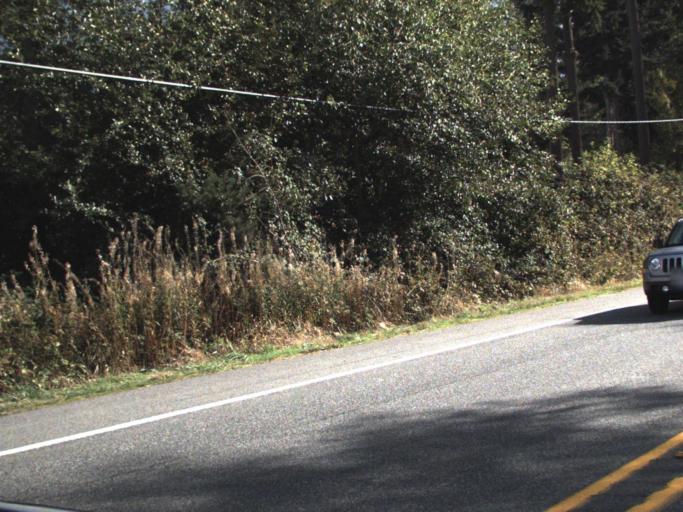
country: US
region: Washington
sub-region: Island County
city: Ault Field
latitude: 48.3646
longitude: -122.6498
